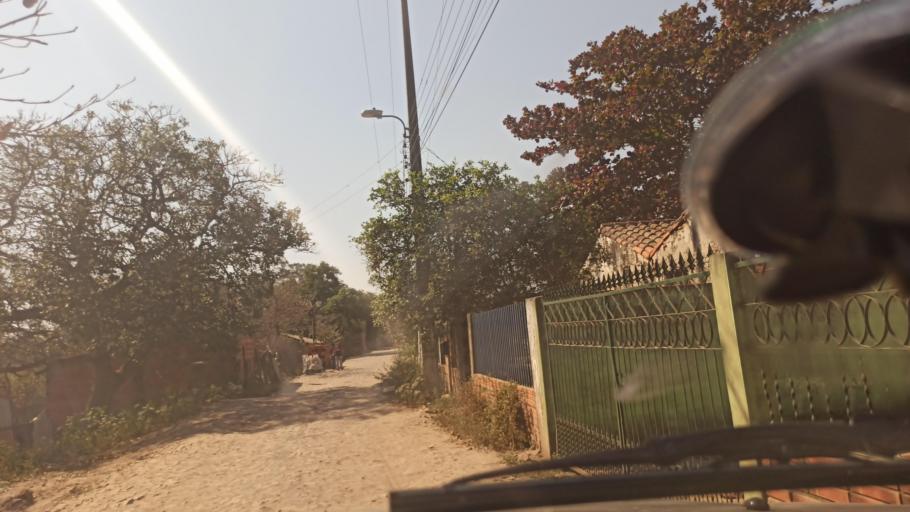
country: AR
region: Formosa
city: Clorinda
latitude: -25.2913
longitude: -57.6964
